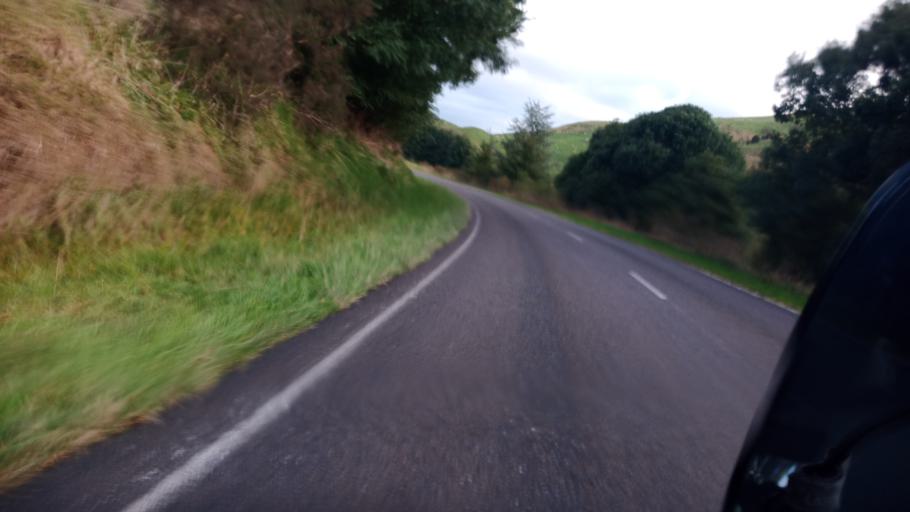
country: NZ
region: Gisborne
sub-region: Gisborne District
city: Gisborne
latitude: -38.5715
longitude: 177.7346
